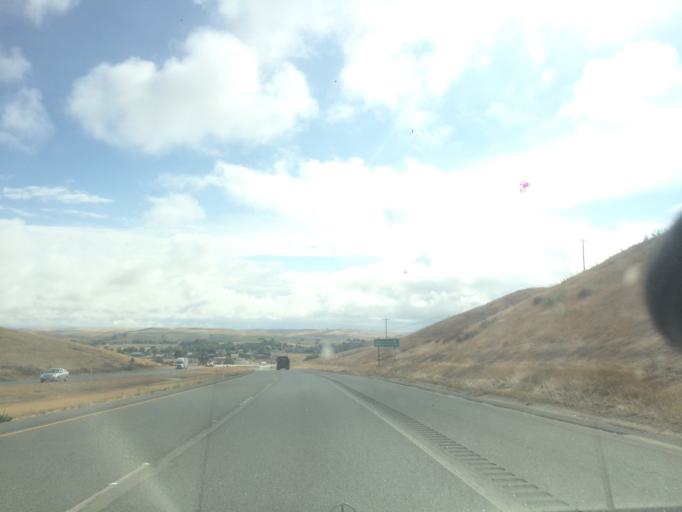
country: US
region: California
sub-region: San Luis Obispo County
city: Shandon
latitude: 35.6556
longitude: -120.5173
